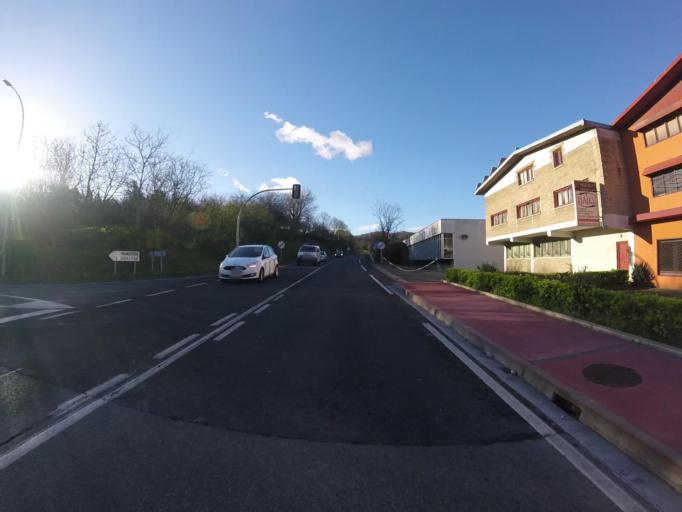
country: ES
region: Basque Country
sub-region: Provincia de Guipuzcoa
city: Errenteria
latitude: 43.2994
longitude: -1.8812
